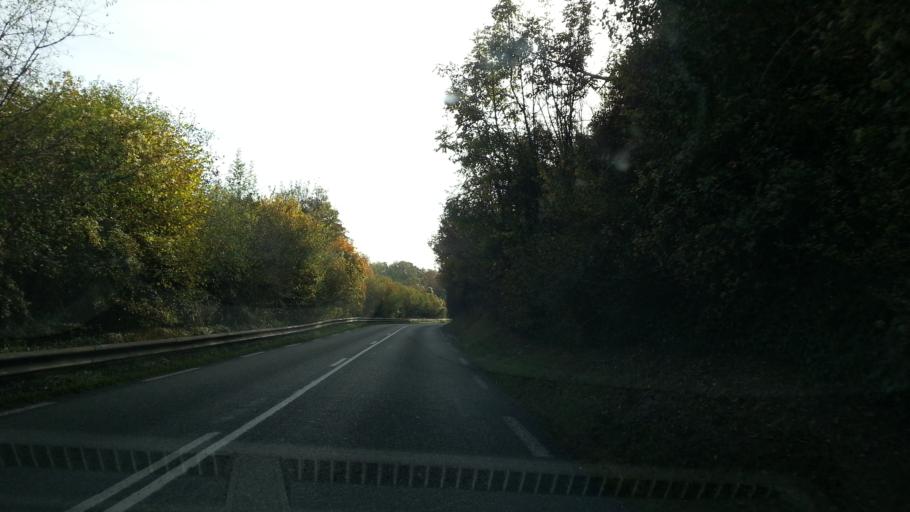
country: FR
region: Picardie
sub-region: Departement de l'Oise
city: Precy-sur-Oise
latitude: 49.1882
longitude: 2.3638
